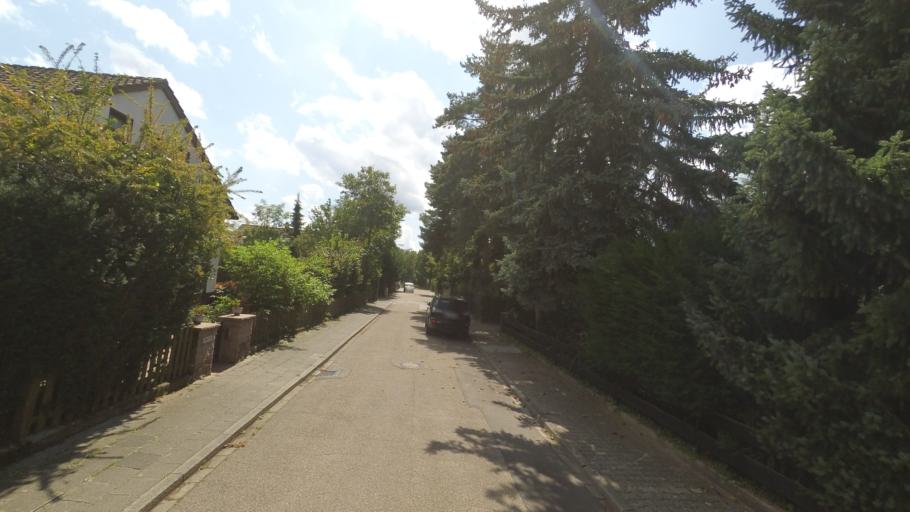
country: DE
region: Rheinland-Pfalz
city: Limburgerhof
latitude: 49.4153
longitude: 8.3844
